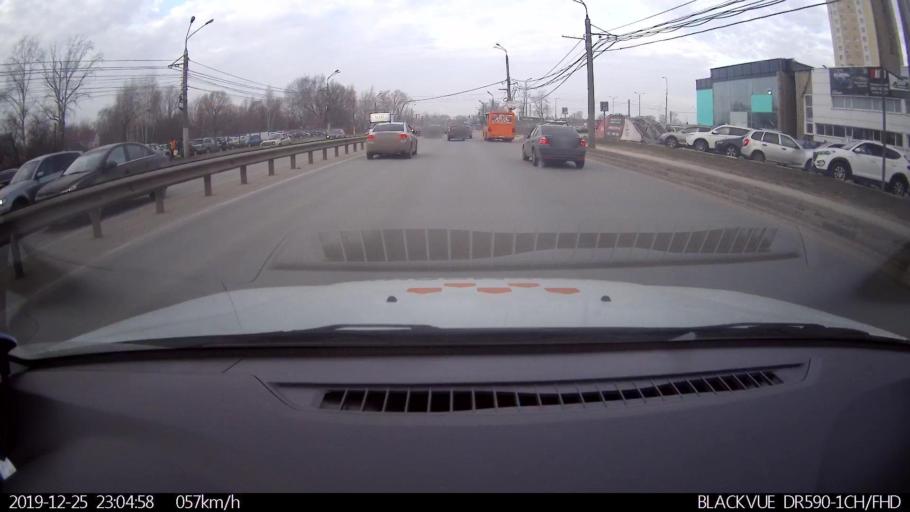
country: RU
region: Nizjnij Novgorod
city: Nizhniy Novgorod
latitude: 56.3013
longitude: 43.9227
